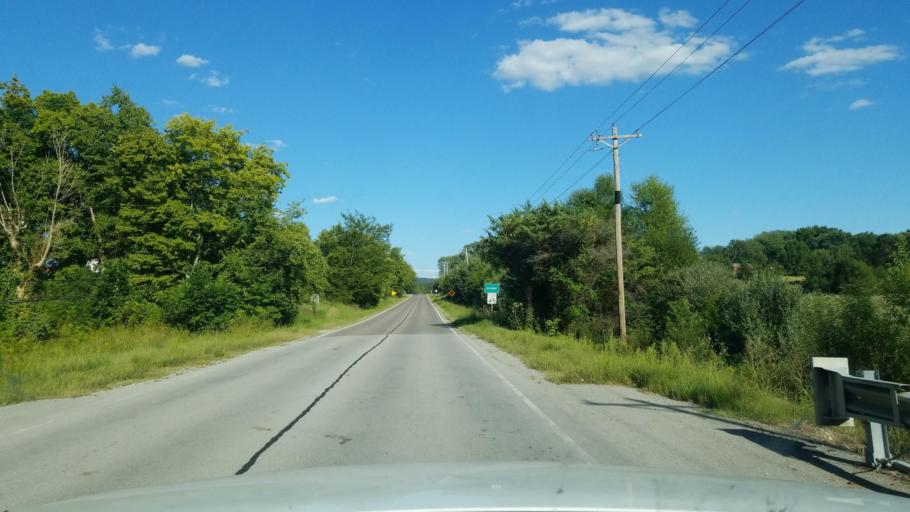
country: US
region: Illinois
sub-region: Saline County
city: Harrisburg
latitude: 37.6364
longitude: -88.4946
